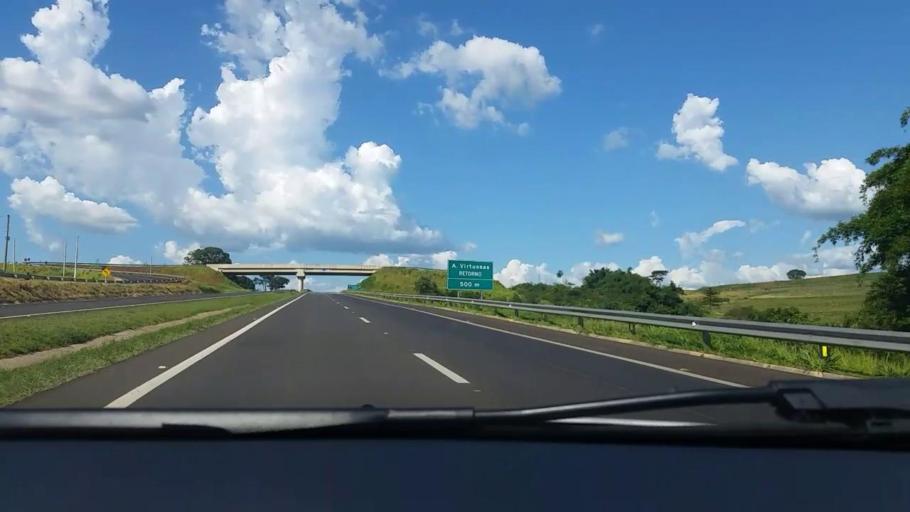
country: BR
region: Sao Paulo
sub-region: Bauru
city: Bauru
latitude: -22.4003
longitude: -49.0900
